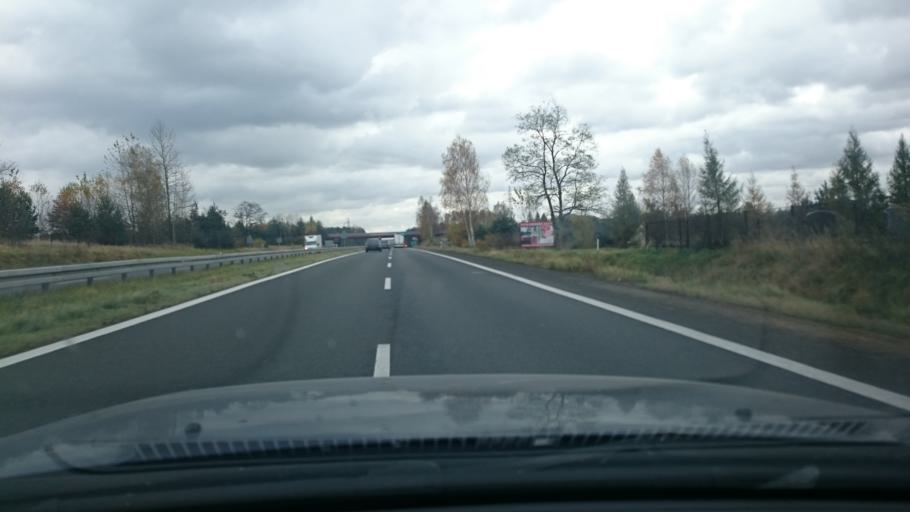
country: PL
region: Lesser Poland Voivodeship
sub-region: Powiat olkuski
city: Boleslaw
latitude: 50.3022
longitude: 19.4887
